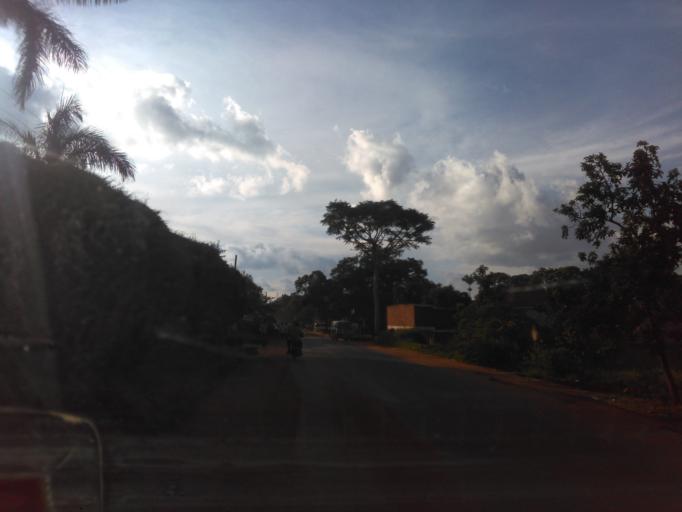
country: UG
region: Central Region
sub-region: Kampala District
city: Kampala
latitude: 0.2600
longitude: 32.5589
